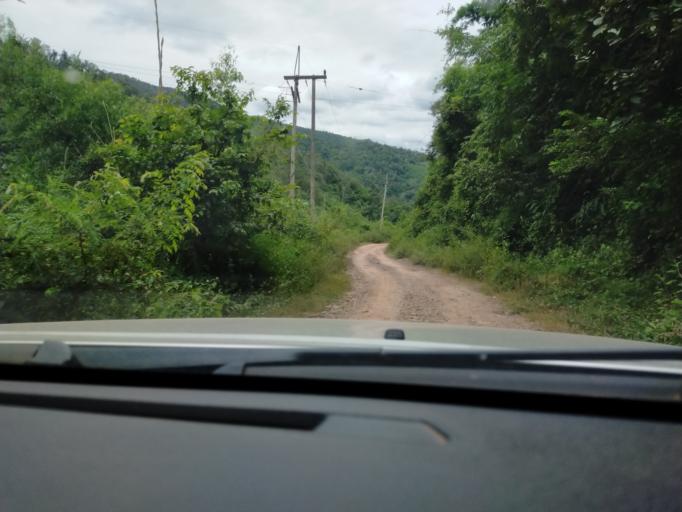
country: TH
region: Nan
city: Chaloem Phra Kiat
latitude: 19.8050
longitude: 101.3623
